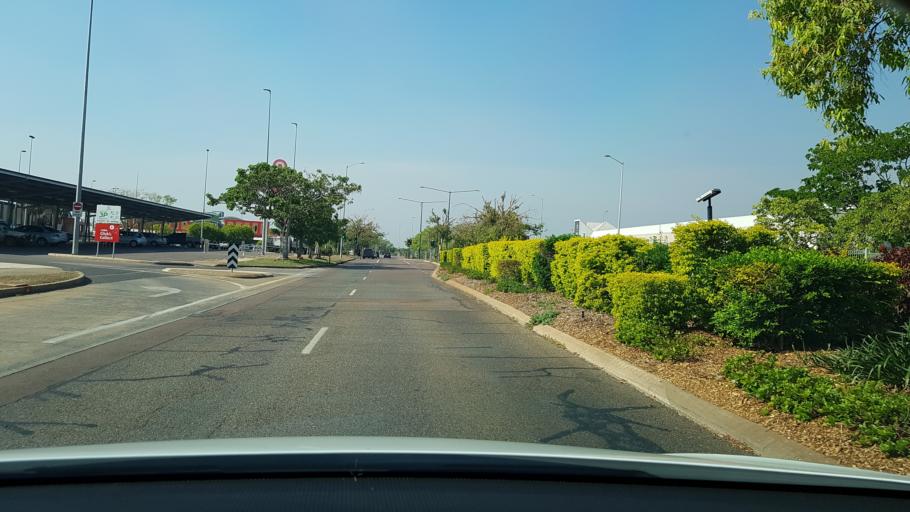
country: AU
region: Northern Territory
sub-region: Palmerston
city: Palmerston
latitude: -12.4815
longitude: 130.9859
